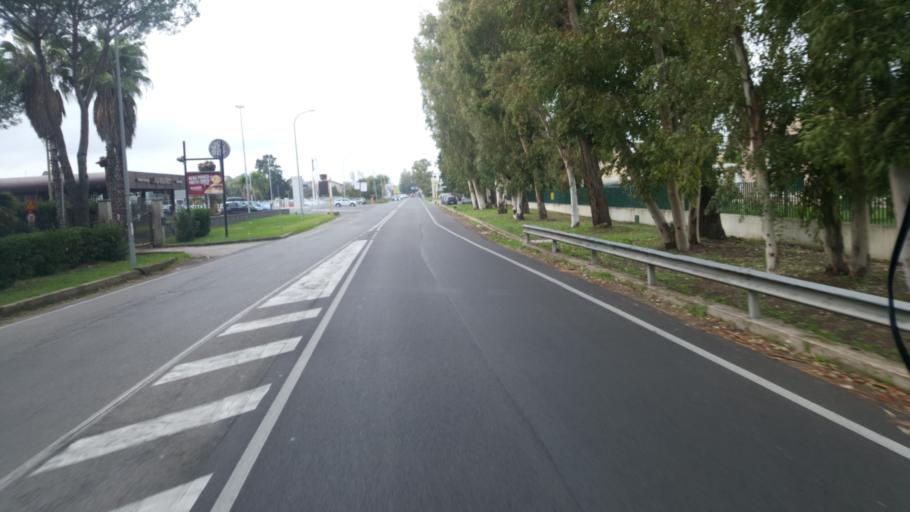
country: IT
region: Latium
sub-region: Provincia di Latina
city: Latina
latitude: 41.4793
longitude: 12.8709
